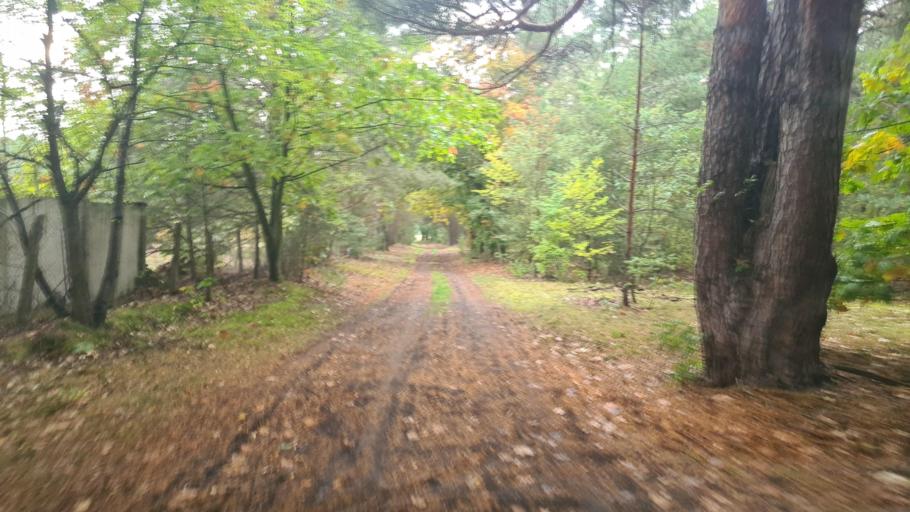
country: DE
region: Brandenburg
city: Storkow
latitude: 52.2252
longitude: 13.9320
